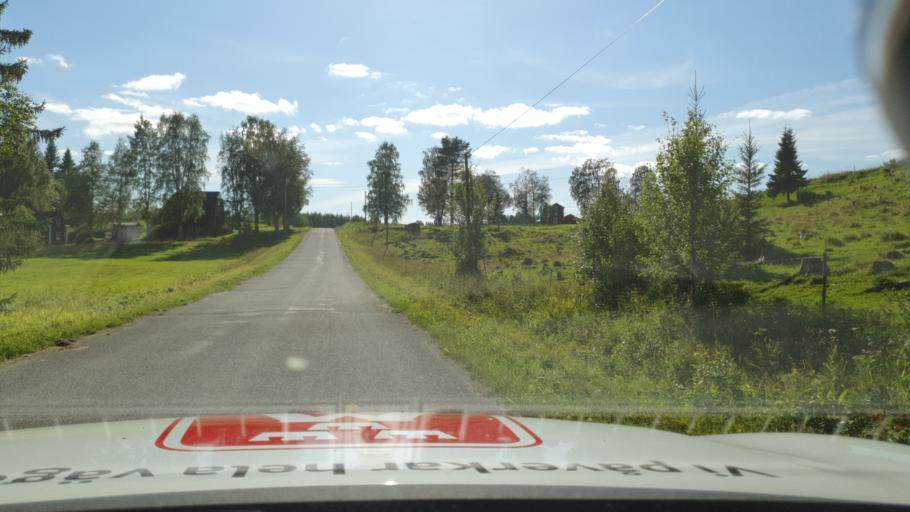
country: SE
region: Jaemtland
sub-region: OEstersunds Kommun
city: Lit
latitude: 63.6642
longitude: 15.0940
